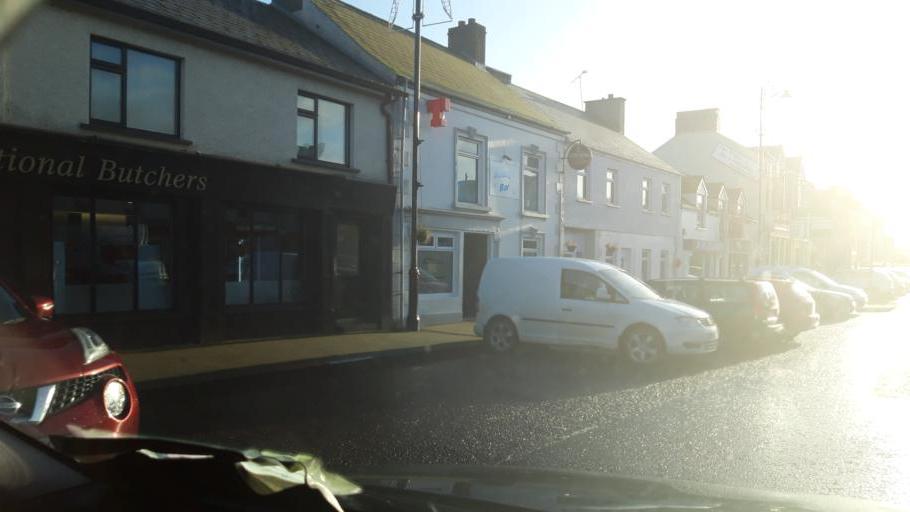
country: GB
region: Northern Ireland
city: Garvagh
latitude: 54.9842
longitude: -6.6871
